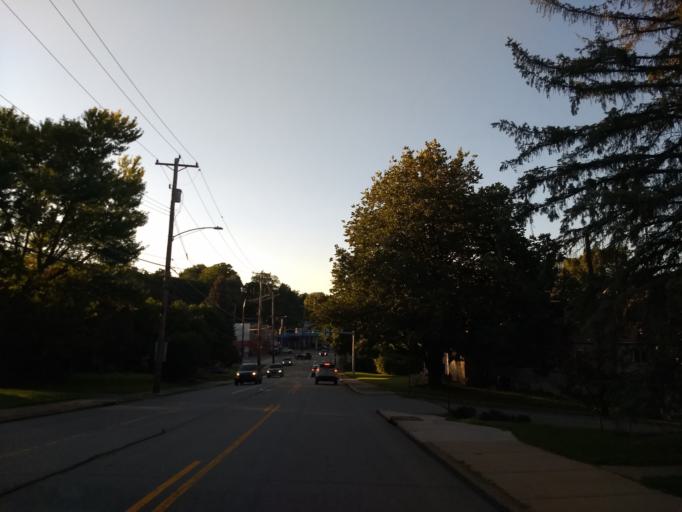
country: US
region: Pennsylvania
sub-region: Allegheny County
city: Mount Lebanon
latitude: 40.3792
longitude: -80.0520
